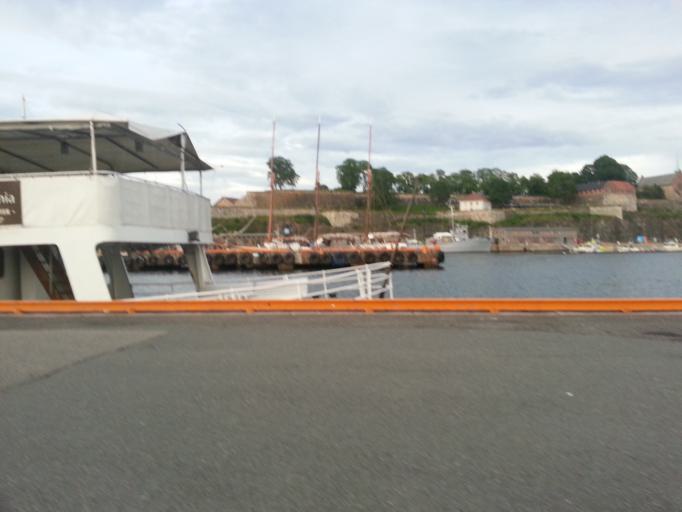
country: NO
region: Oslo
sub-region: Oslo
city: Oslo
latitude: 59.9098
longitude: 10.7311
